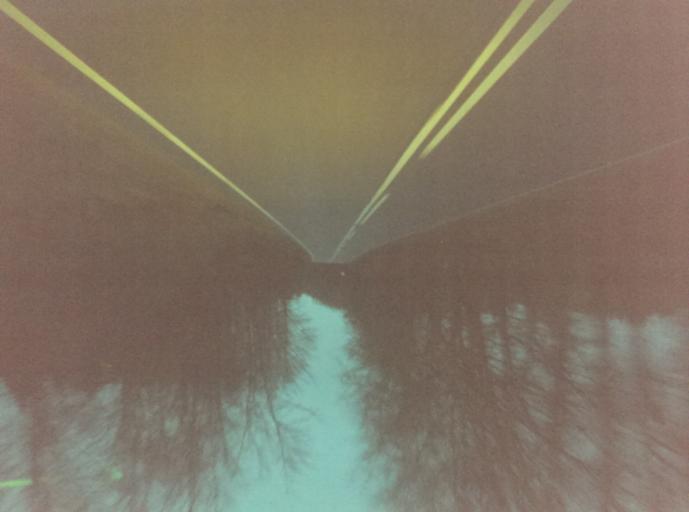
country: DK
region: South Denmark
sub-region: Esbjerg Kommune
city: Tjaereborg
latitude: 55.4844
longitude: 8.5794
